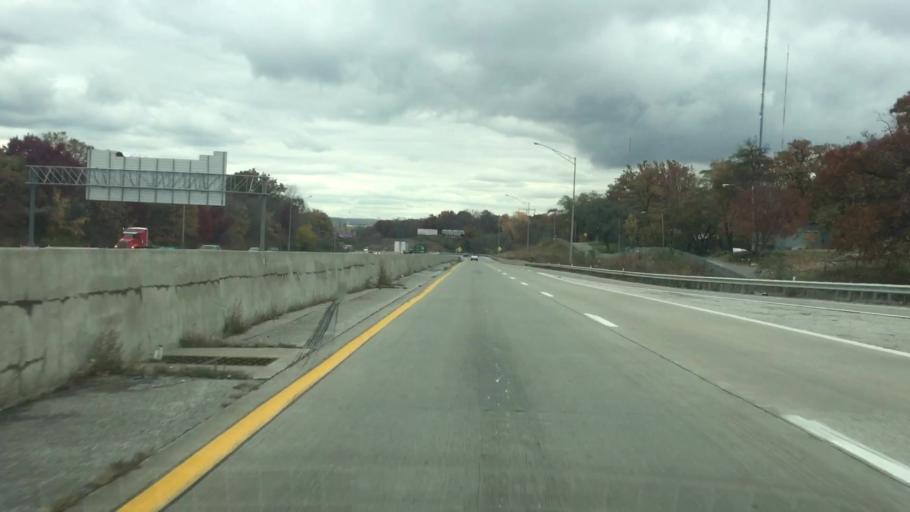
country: US
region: Missouri
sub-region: Jackson County
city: Sugar Creek
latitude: 39.0674
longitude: -94.4878
